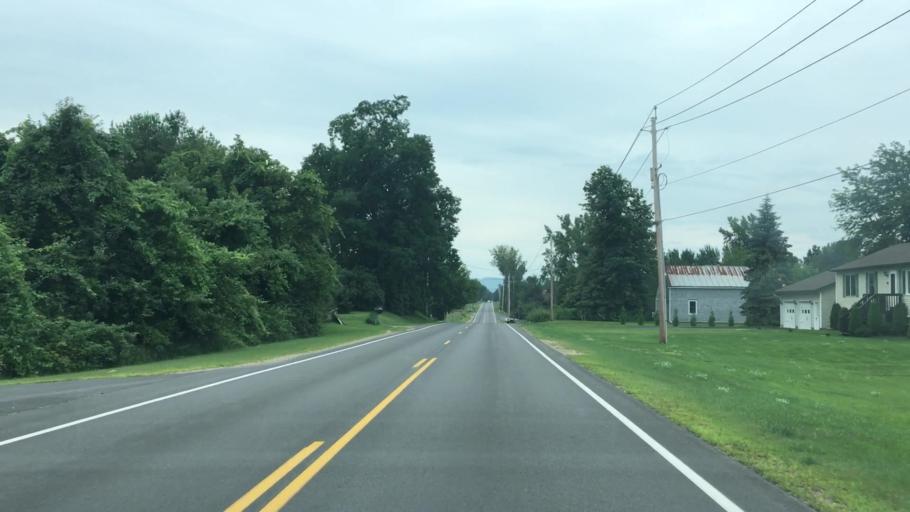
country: US
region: New York
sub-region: Clinton County
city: Peru
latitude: 44.5936
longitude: -73.5727
